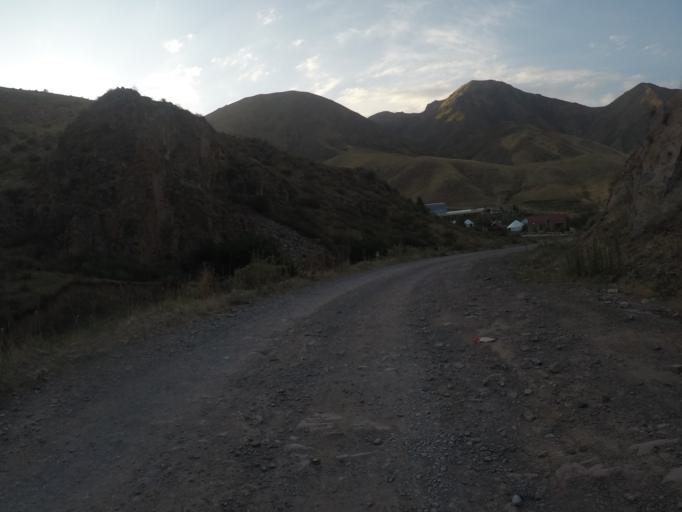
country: KG
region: Chuy
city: Bishkek
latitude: 42.6696
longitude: 74.6454
